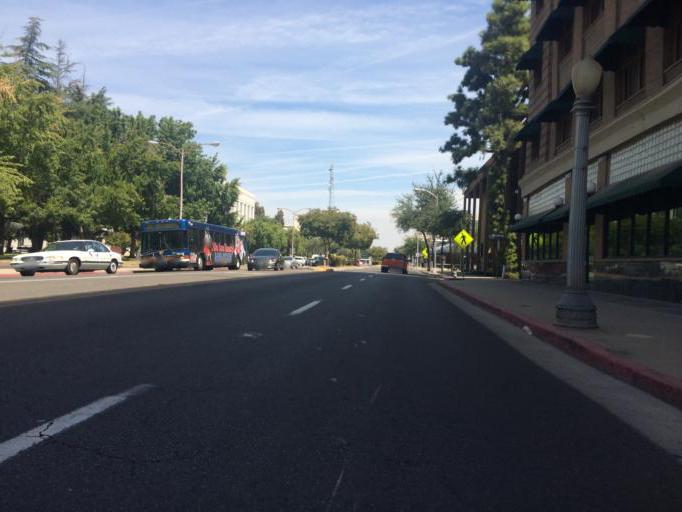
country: US
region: California
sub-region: Fresno County
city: Fresno
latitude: 36.7347
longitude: -119.7890
